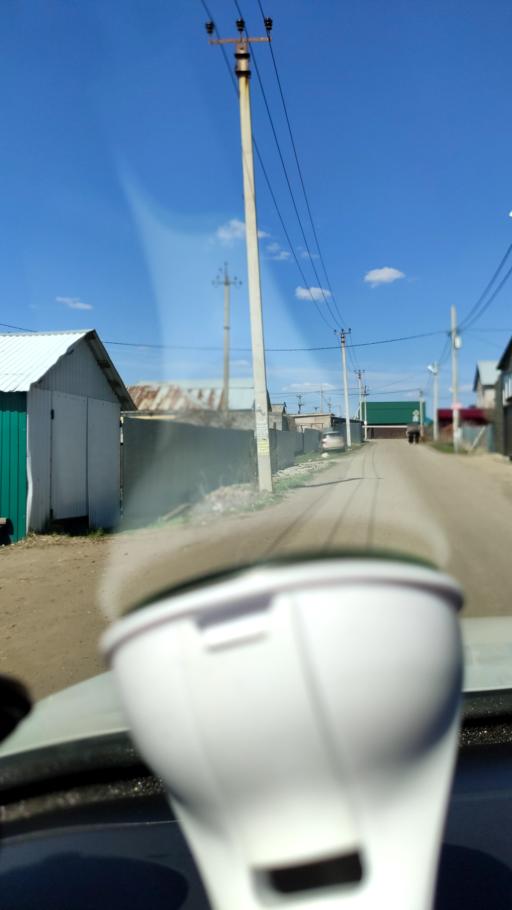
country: RU
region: Samara
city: Smyshlyayevka
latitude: 53.2636
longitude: 50.4180
